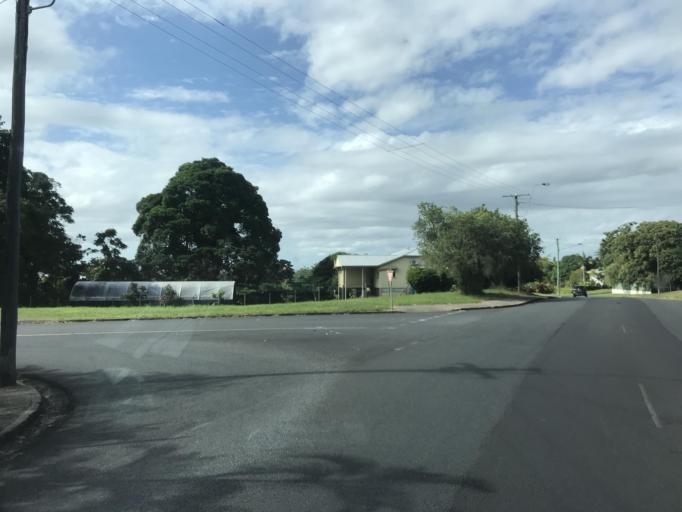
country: AU
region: Queensland
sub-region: Cassowary Coast
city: Innisfail
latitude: -17.5305
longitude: 146.0346
